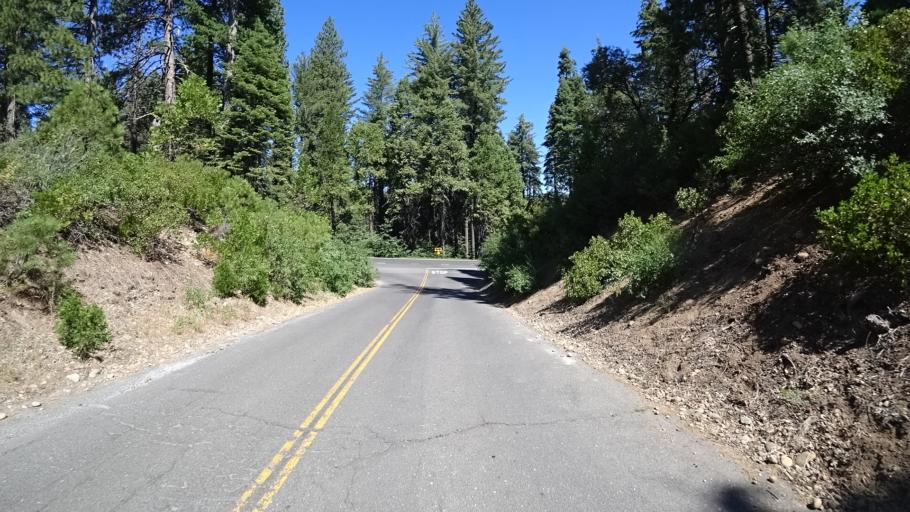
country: US
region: California
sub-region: Calaveras County
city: Arnold
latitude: 38.2960
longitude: -120.2836
